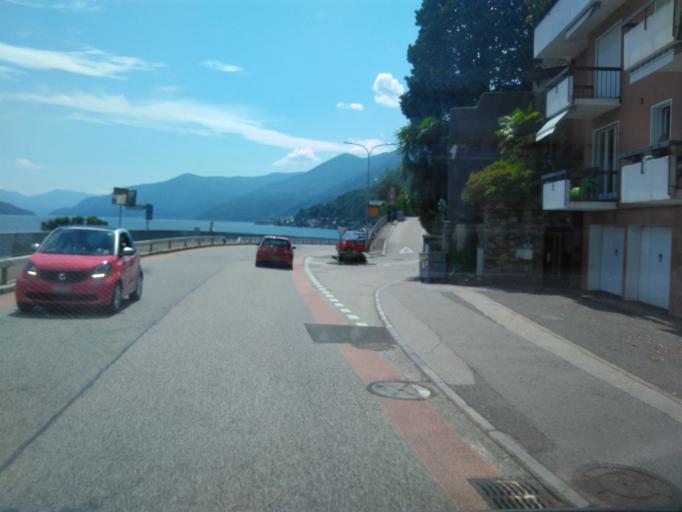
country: CH
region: Ticino
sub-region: Locarno District
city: Brissago
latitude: 46.1424
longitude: 8.7285
